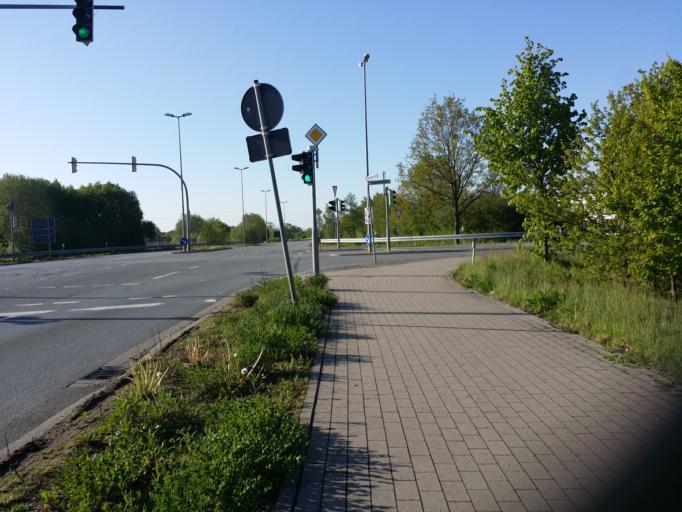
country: DE
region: Bremen
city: Bremen
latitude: 53.0207
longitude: 8.8660
